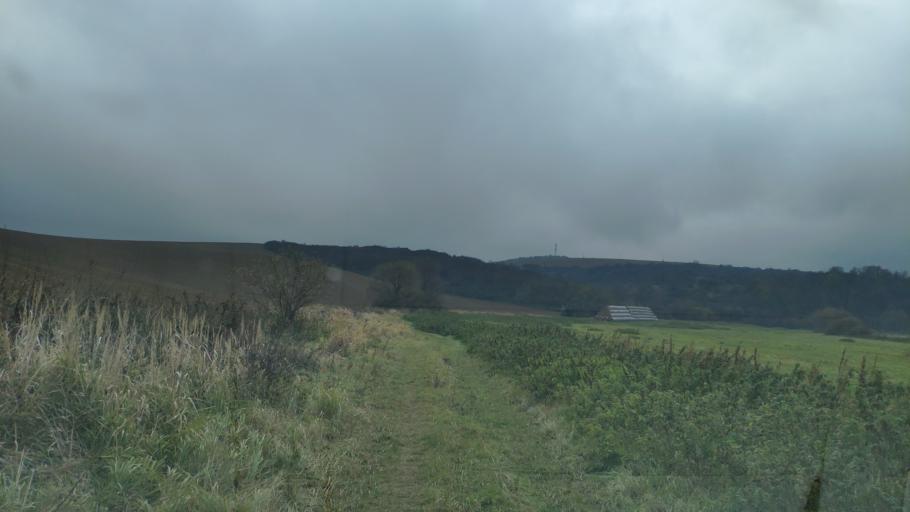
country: SK
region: Presovsky
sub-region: Okres Presov
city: Presov
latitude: 49.0162
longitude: 21.2007
